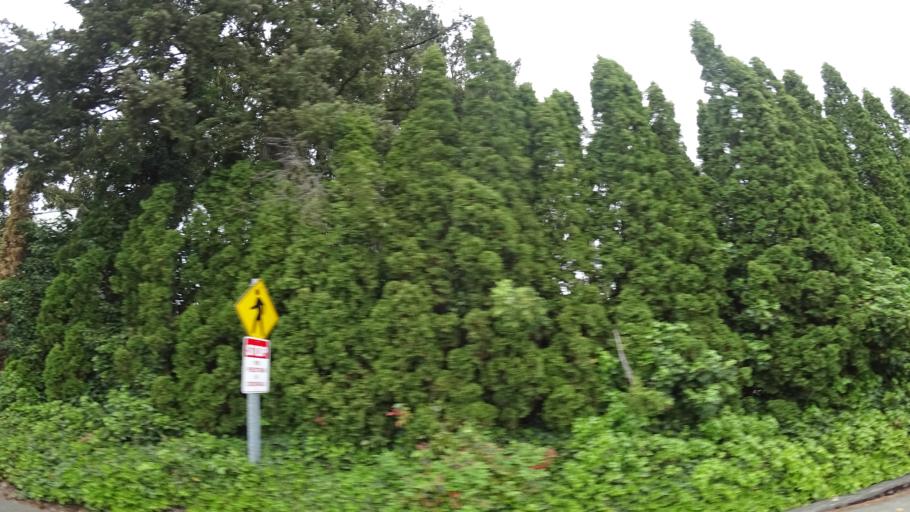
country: US
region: Oregon
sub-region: Washington County
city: Tigard
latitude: 45.4479
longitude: -122.7796
